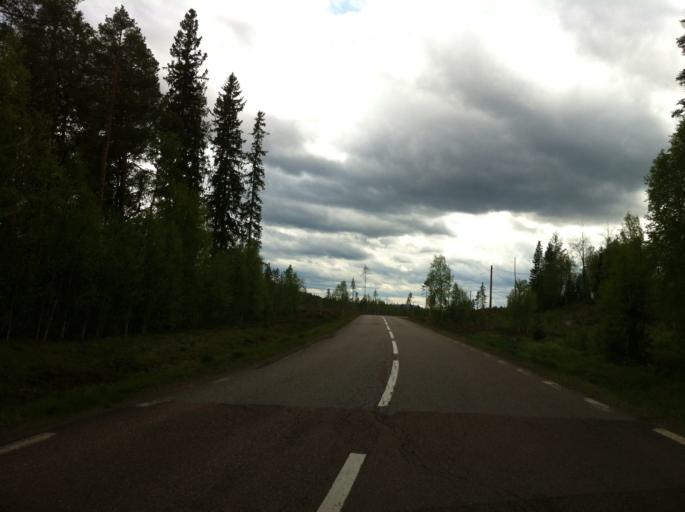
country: NO
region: Hedmark
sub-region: Trysil
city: Innbygda
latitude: 61.4345
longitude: 13.0967
